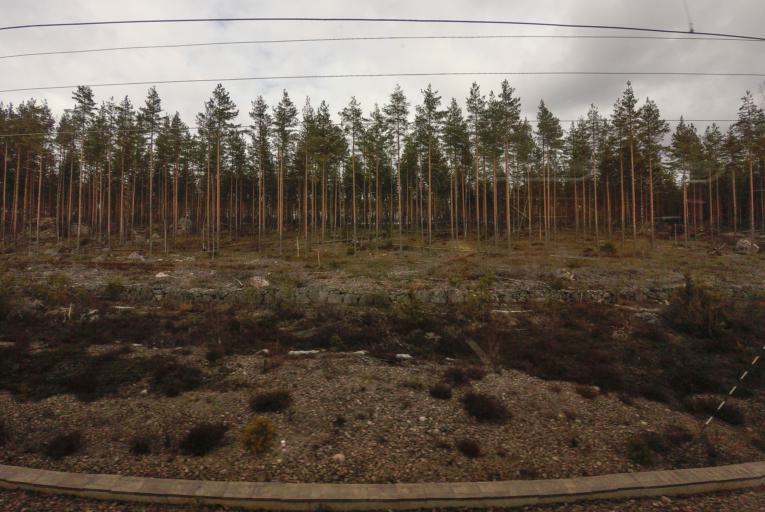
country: FI
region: Paijanne Tavastia
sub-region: Lahti
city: Artjaervi
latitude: 60.9245
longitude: 26.1249
